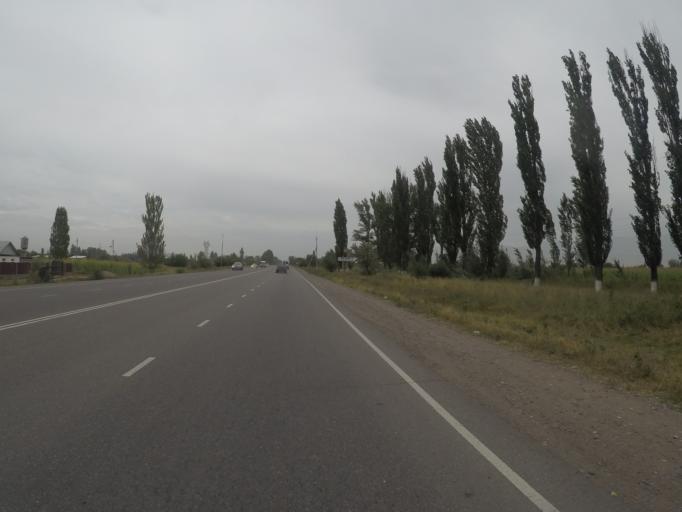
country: KG
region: Chuy
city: Bystrovka
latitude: 42.8202
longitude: 75.5705
